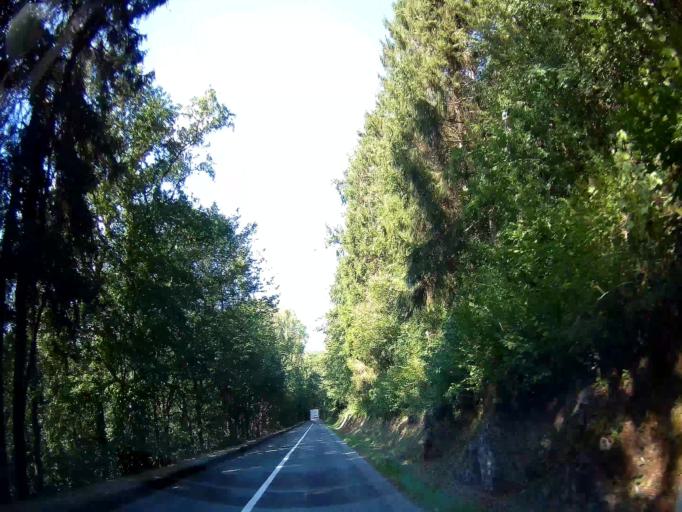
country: BE
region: Wallonia
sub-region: Province de Namur
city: Onhaye
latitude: 50.3037
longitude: 4.7626
